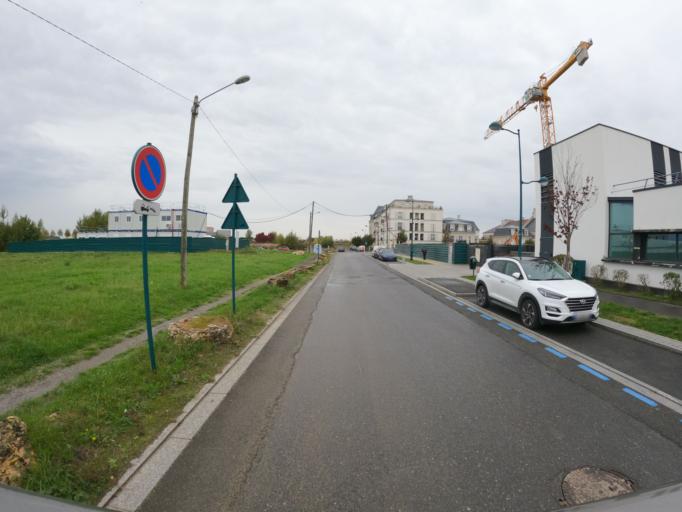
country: FR
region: Ile-de-France
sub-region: Departement de Seine-et-Marne
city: Serris
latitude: 48.8578
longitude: 2.7830
